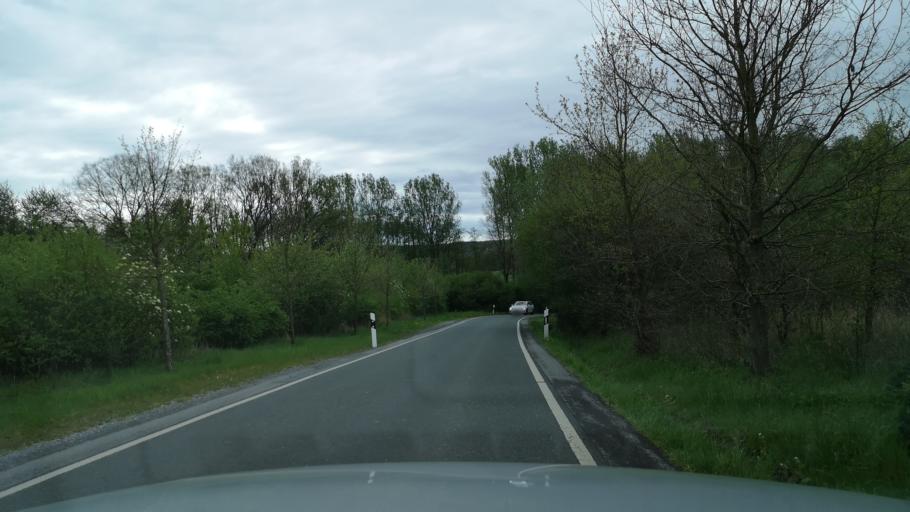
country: DE
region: North Rhine-Westphalia
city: Iserlohn
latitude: 51.4421
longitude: 7.7105
